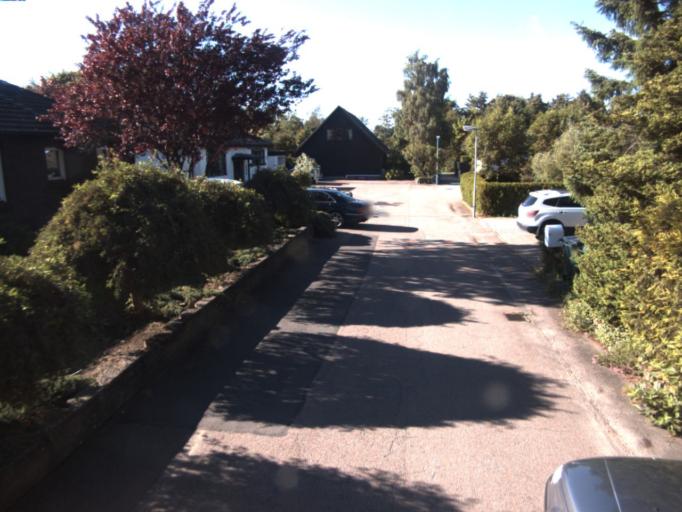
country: SE
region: Skane
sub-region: Helsingborg
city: Odakra
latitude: 56.1026
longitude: 12.7610
